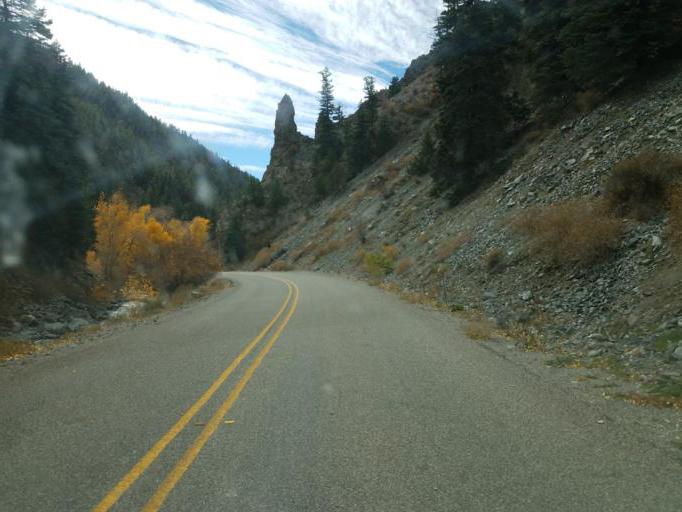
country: US
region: New Mexico
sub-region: Taos County
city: Arroyo Seco
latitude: 36.5476
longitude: -105.5519
